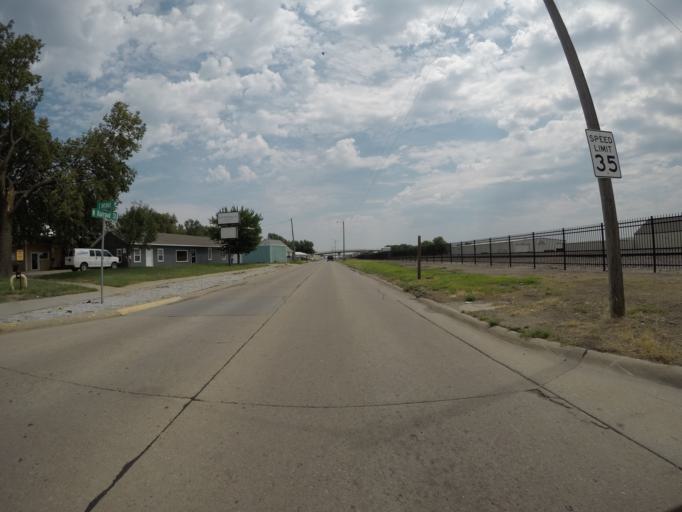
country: US
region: Nebraska
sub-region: Buffalo County
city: Kearney
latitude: 40.6962
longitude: -99.0775
